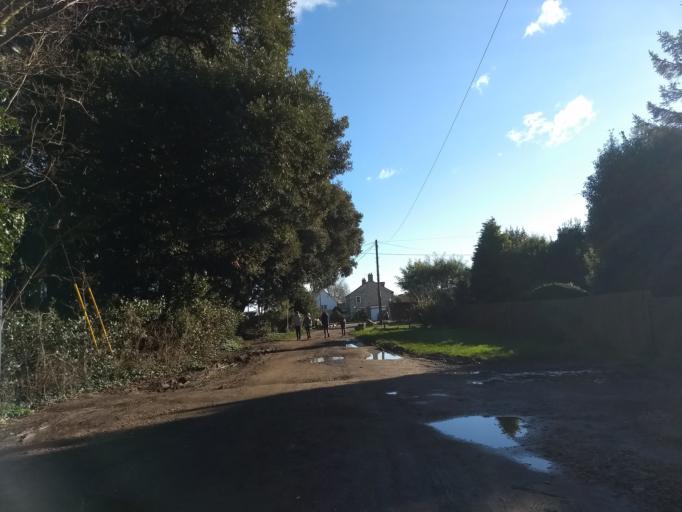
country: GB
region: England
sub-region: Isle of Wight
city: Bembridge
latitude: 50.6858
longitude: -1.0739
